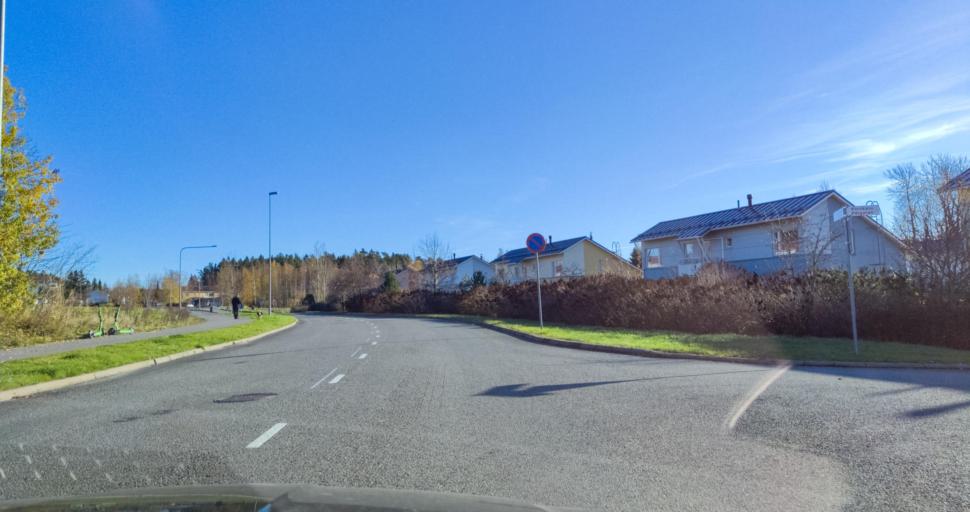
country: FI
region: Varsinais-Suomi
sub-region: Turku
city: Turku
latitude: 60.4092
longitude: 22.2180
